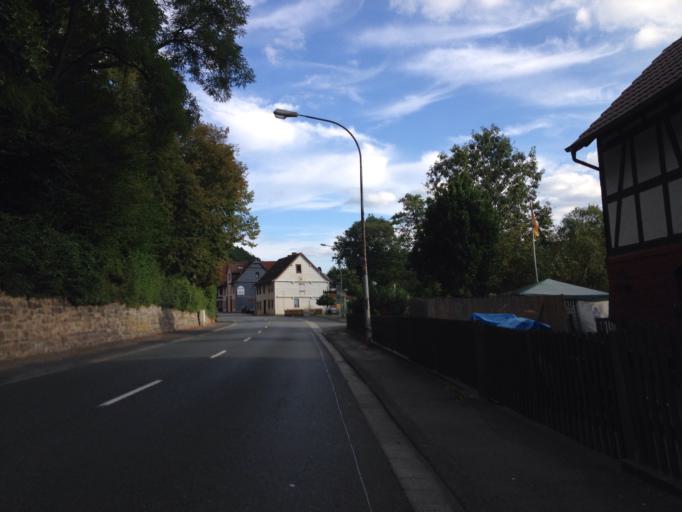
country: DE
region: Hesse
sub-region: Regierungsbezirk Giessen
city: Biedenkopf
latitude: 50.9219
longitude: 8.5047
